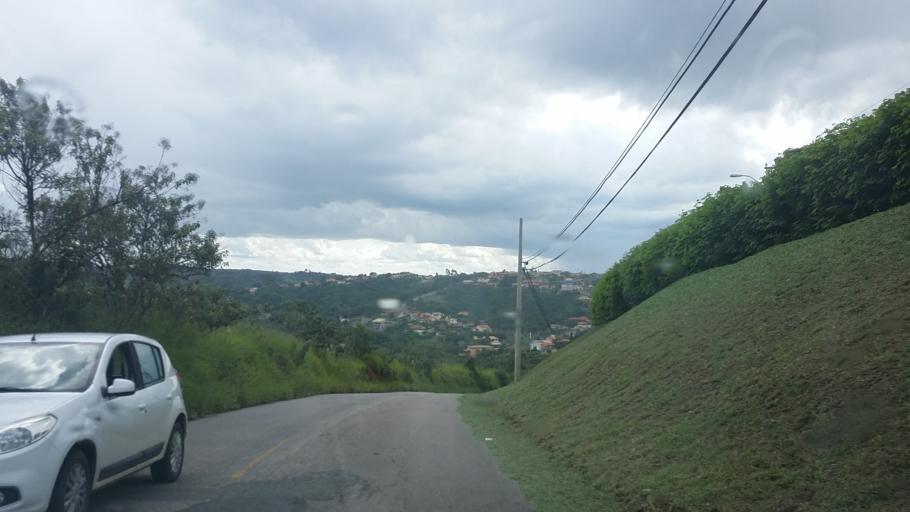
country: BR
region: Sao Paulo
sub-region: Itupeva
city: Itupeva
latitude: -23.1675
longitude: -47.0983
